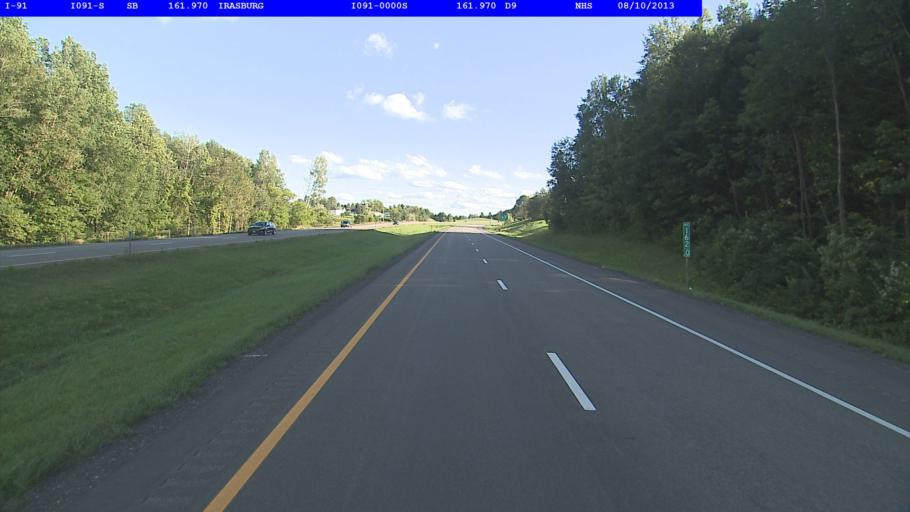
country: US
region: Vermont
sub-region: Orleans County
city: Newport
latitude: 44.8145
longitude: -72.2110
